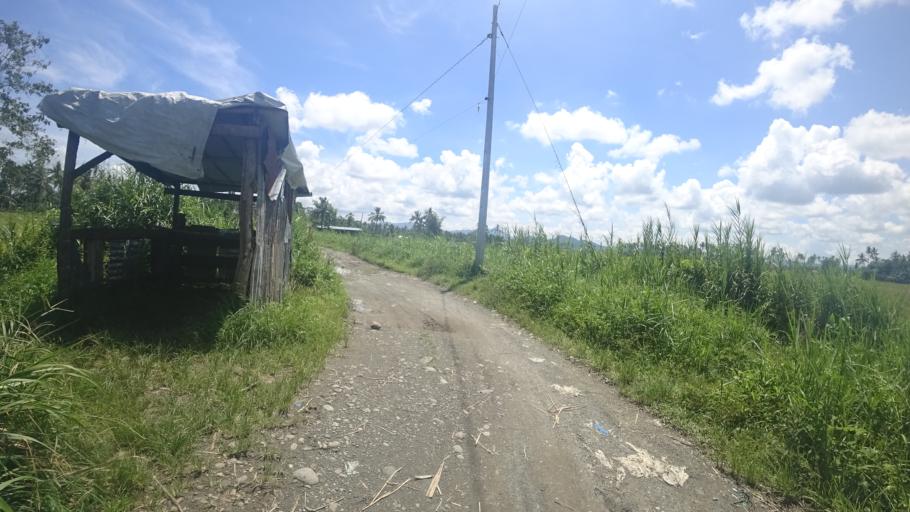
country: PH
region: Eastern Visayas
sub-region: Province of Leyte
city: Alangalang
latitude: 11.2315
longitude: 124.8447
